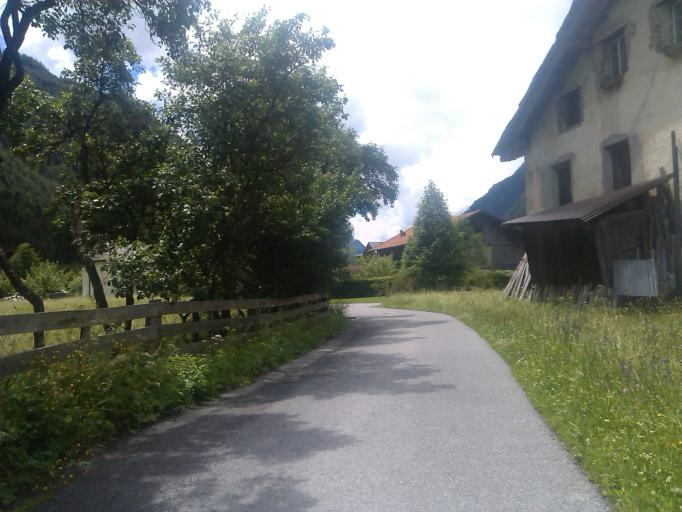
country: AT
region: Tyrol
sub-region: Politischer Bezirk Landeck
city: Fiss
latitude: 47.0302
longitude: 10.6272
